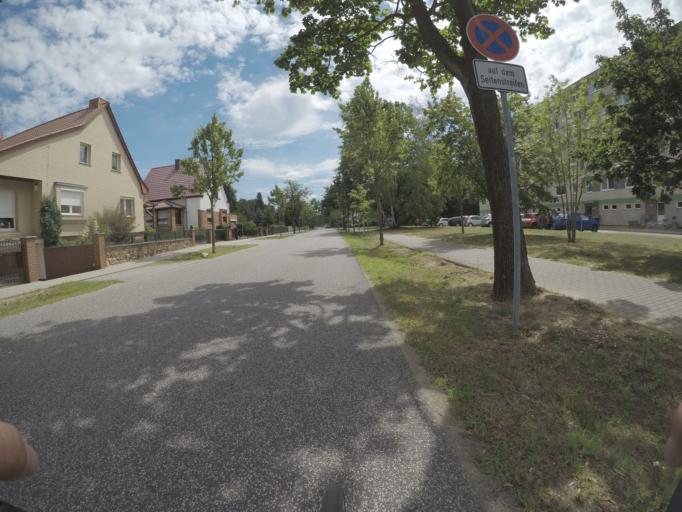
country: DE
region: Brandenburg
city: Storkow
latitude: 52.2480
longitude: 13.9469
